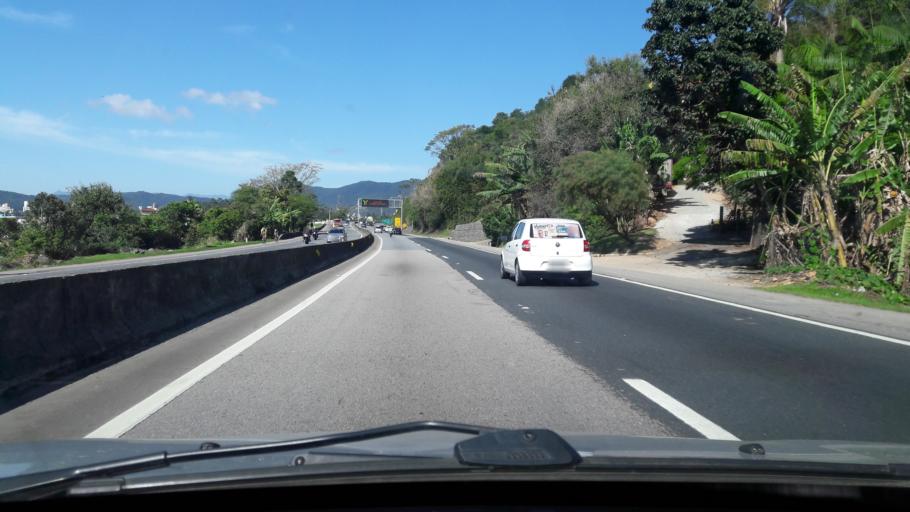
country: BR
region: Santa Catarina
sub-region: Biguacu
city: Biguacu
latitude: -27.4827
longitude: -48.6468
